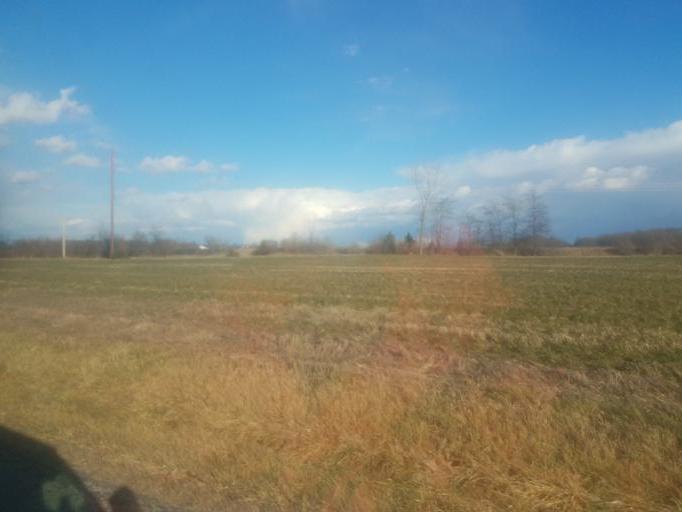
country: US
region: Ohio
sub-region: Marion County
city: Prospect
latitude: 40.3989
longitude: -83.1446
